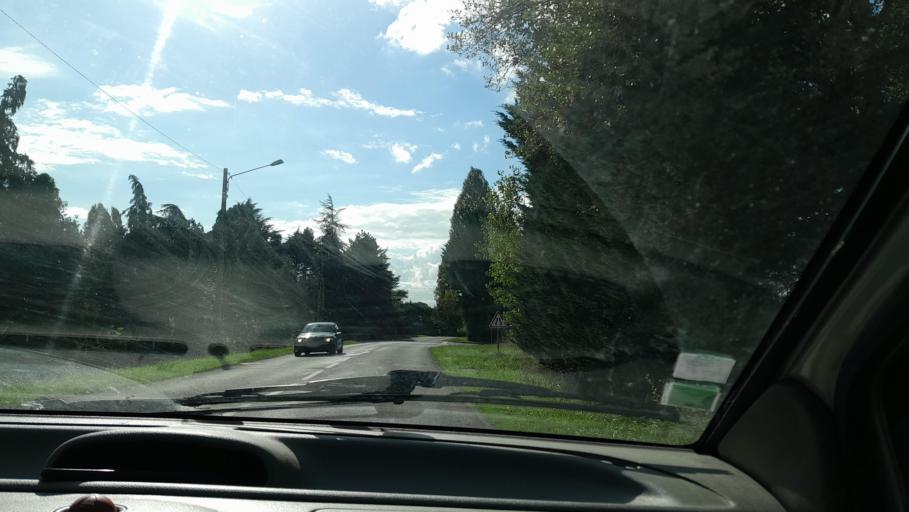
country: FR
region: Pays de la Loire
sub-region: Departement de la Mayenne
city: Saint-Berthevin
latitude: 48.0544
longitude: -0.8025
